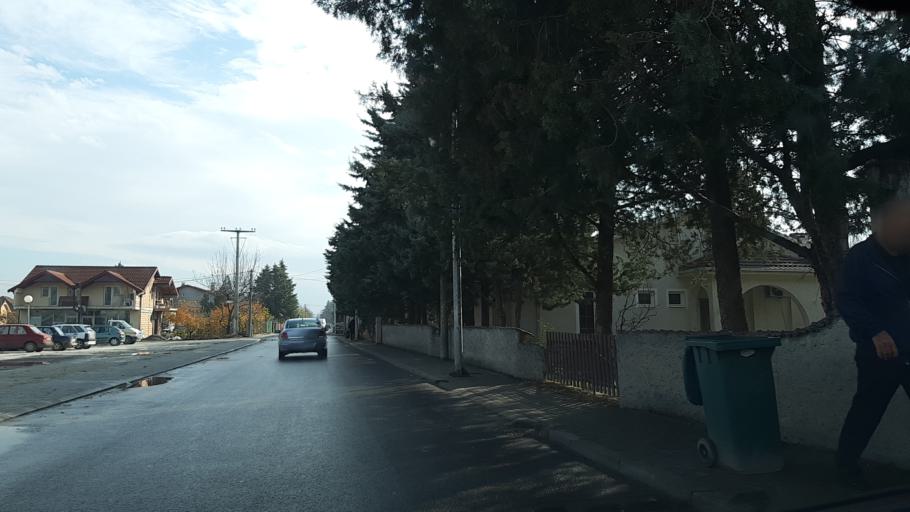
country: MK
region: Kisela Voda
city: Usje
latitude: 41.9790
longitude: 21.4813
